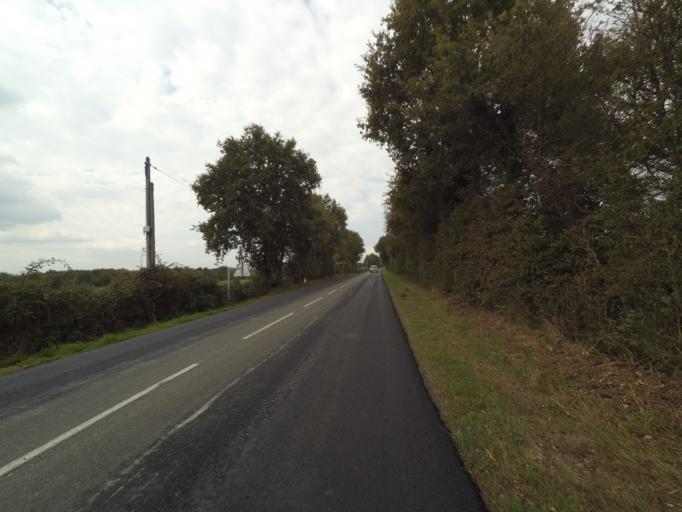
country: FR
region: Pays de la Loire
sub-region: Departement de la Vendee
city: Bouffere
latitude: 46.9854
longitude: -1.3562
